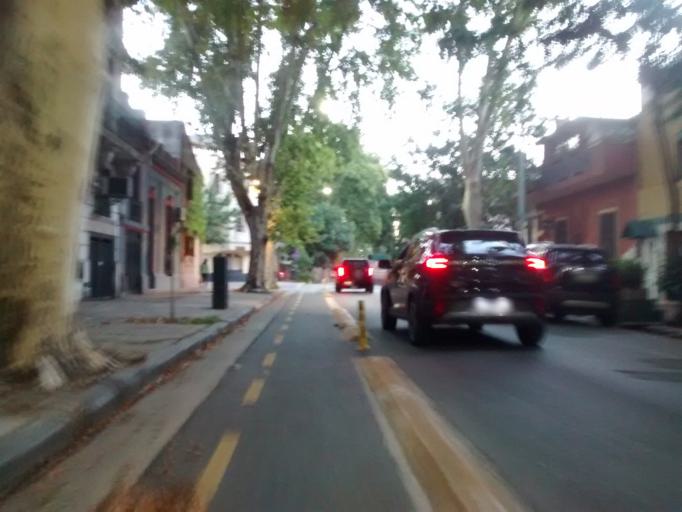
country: AR
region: Buenos Aires F.D.
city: Villa Santa Rita
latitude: -34.6063
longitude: -58.4549
